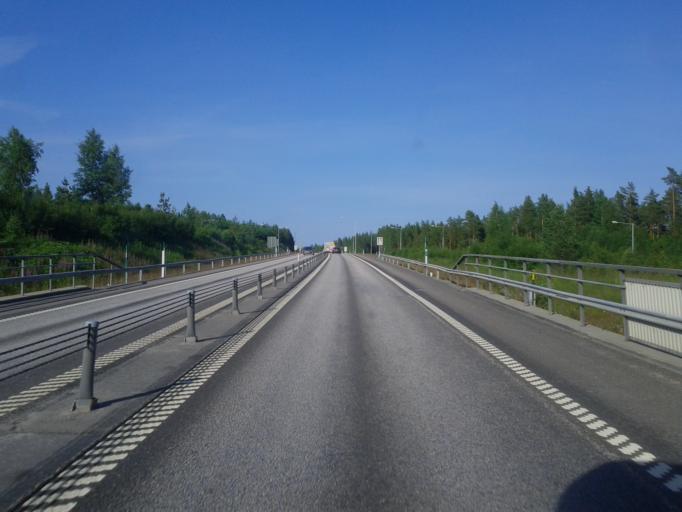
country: SE
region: Vaesterbotten
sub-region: Umea Kommun
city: Saevar
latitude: 63.8991
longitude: 20.5646
